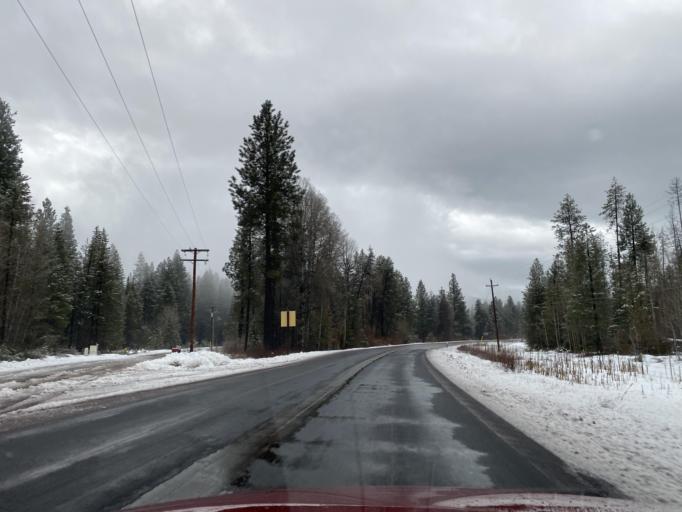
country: US
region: Oregon
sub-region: Klamath County
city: Klamath Falls
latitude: 42.4400
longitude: -122.1177
